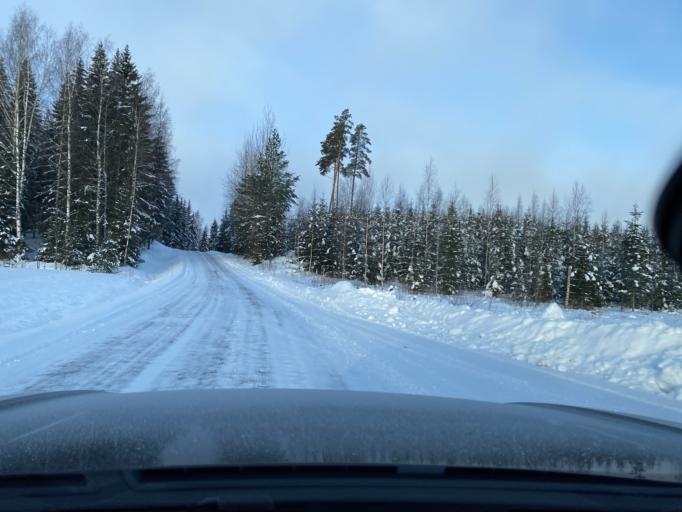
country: FI
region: Haeme
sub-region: Forssa
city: Tammela
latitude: 60.8607
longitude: 23.9004
